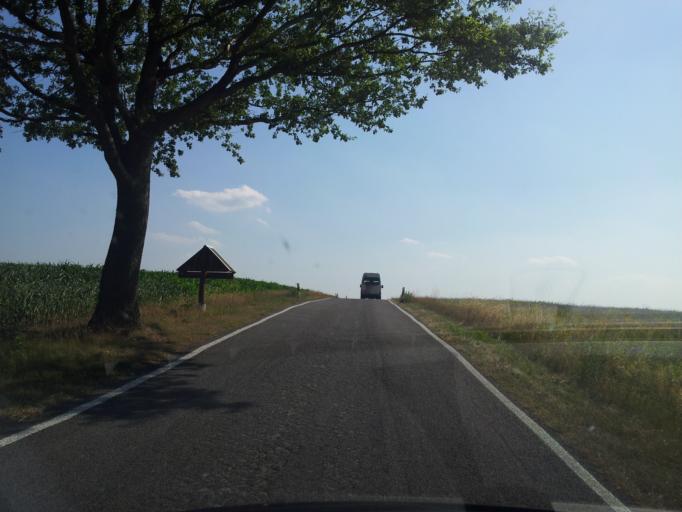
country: DE
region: Saxony
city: Hockendorf
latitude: 51.2204
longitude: 13.9114
